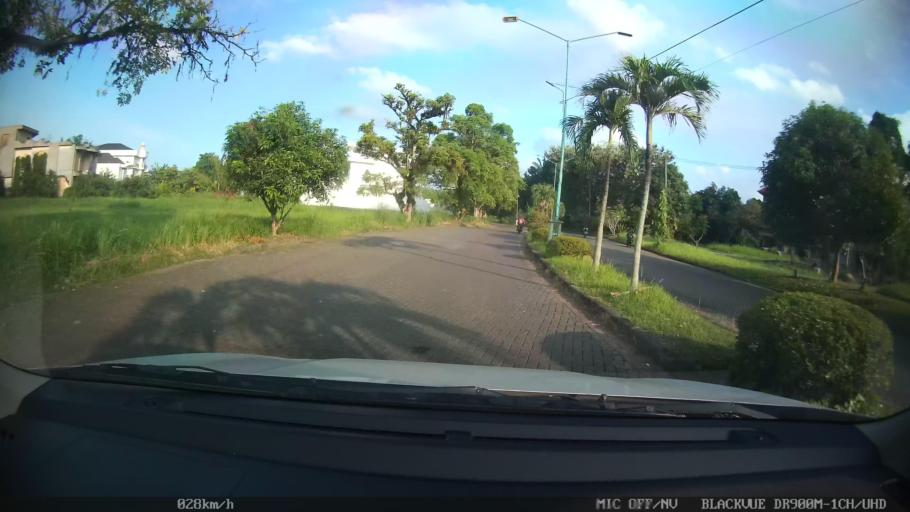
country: ID
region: North Sumatra
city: Medan
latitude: 3.6260
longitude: 98.6474
